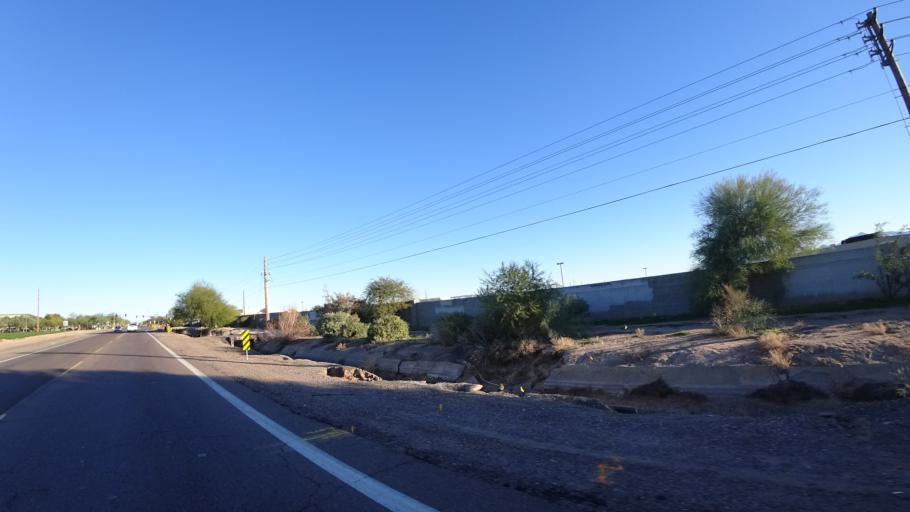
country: US
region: Arizona
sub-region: Maricopa County
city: Tolleson
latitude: 33.4518
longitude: -112.2323
